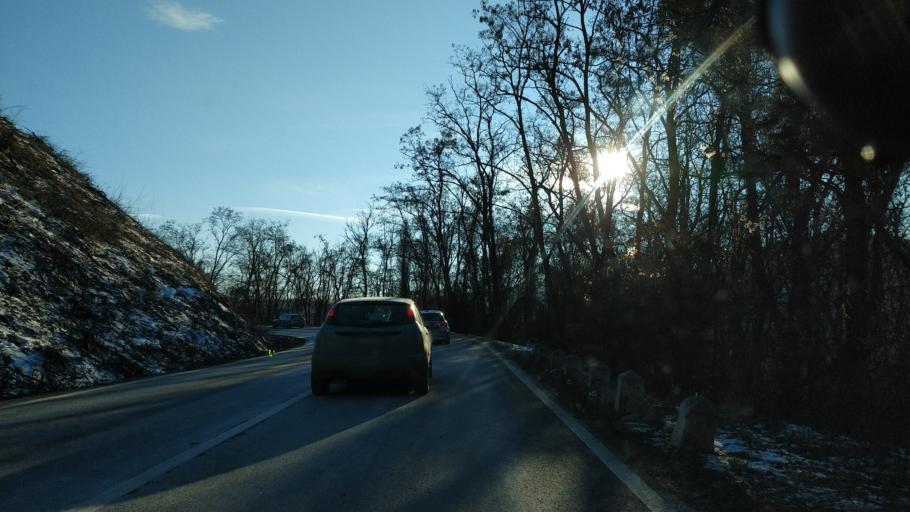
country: RO
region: Bacau
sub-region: Comuna Luizi-Calugara
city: Luizi-Calugara
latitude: 46.5443
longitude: 26.8179
